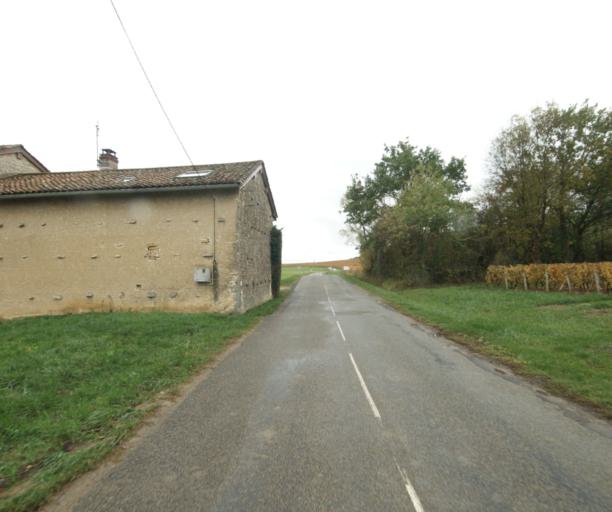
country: FR
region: Bourgogne
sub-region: Departement de Saone-et-Loire
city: Saint-Martin-Belle-Roche
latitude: 46.4684
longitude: 4.8514
